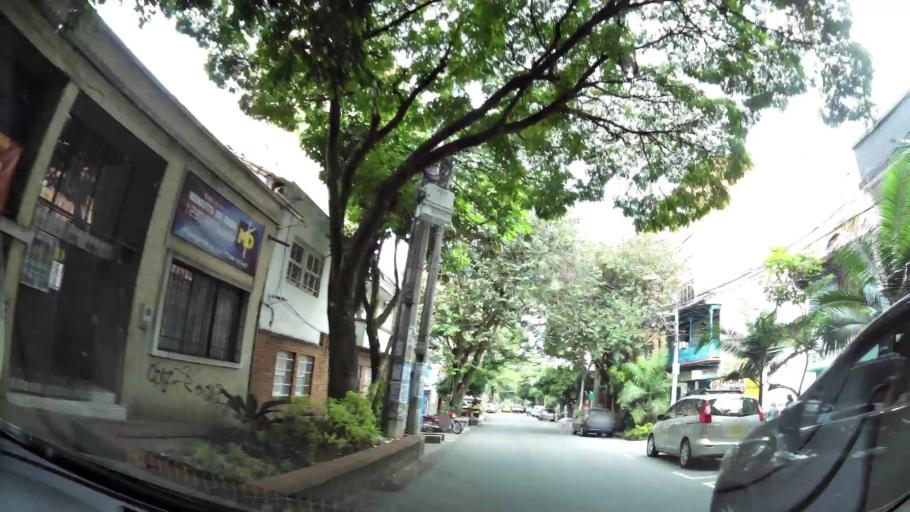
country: CO
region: Antioquia
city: Medellin
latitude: 6.2508
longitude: -75.5597
